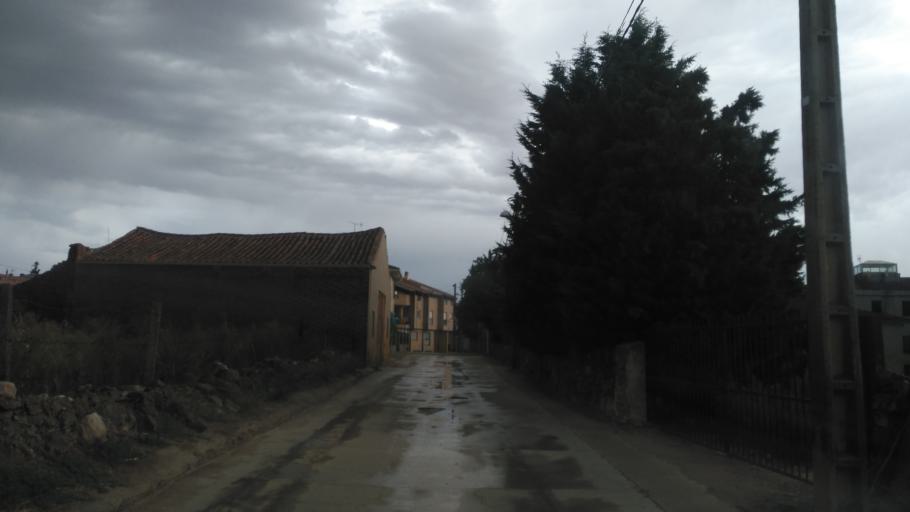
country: ES
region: Castille and Leon
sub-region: Provincia de Salamanca
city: Aldeatejada
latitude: 40.9208
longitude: -5.6918
